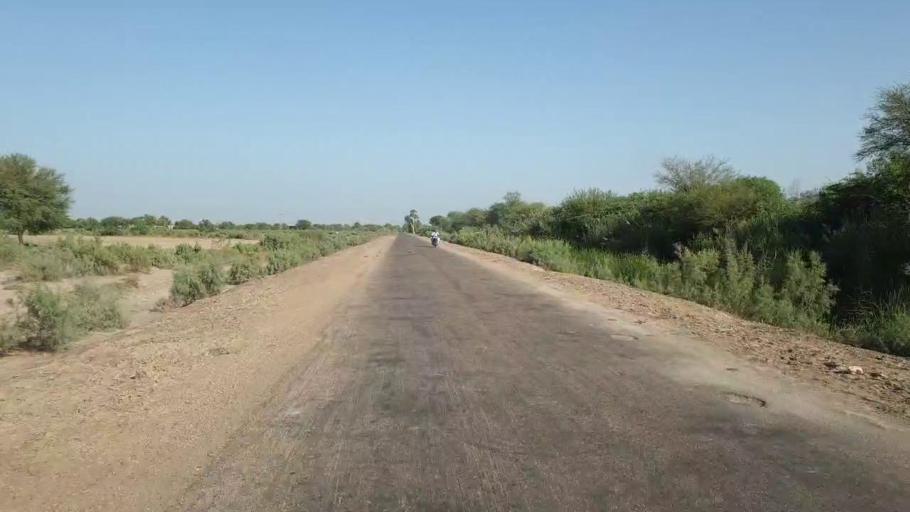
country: PK
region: Sindh
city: Nawabshah
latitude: 26.3861
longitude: 68.4537
